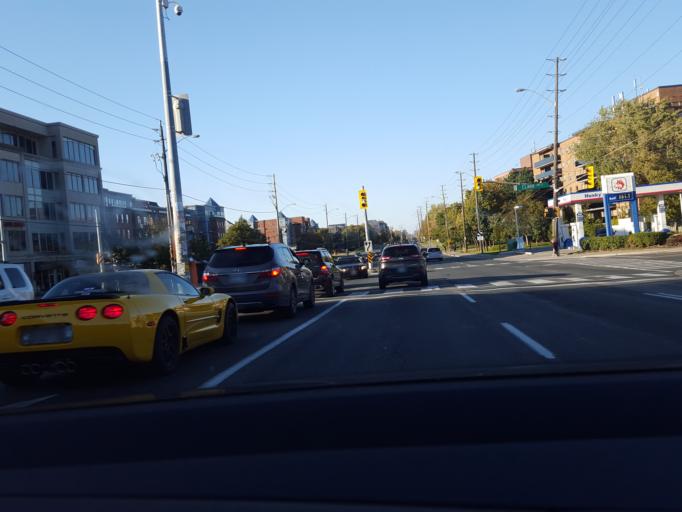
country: CA
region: Ontario
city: North York
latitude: 43.8068
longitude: -79.4223
